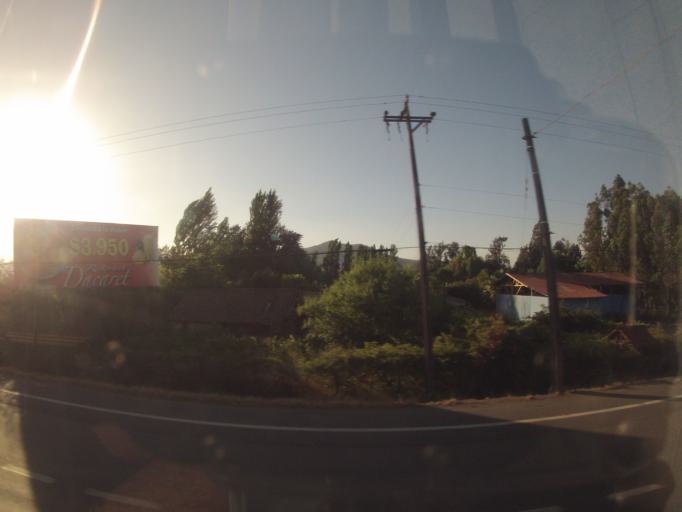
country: CL
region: O'Higgins
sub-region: Provincia de Colchagua
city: Chimbarongo
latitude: -34.6976
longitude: -71.0203
